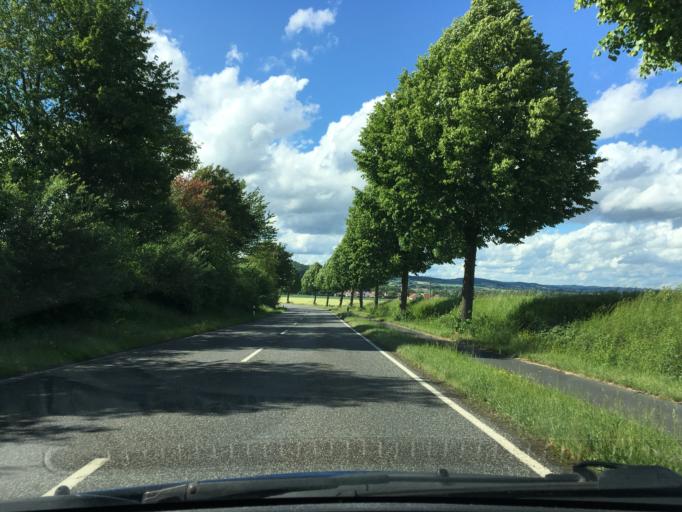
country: DE
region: Lower Saxony
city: Bovenden
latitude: 51.5924
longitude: 9.8686
